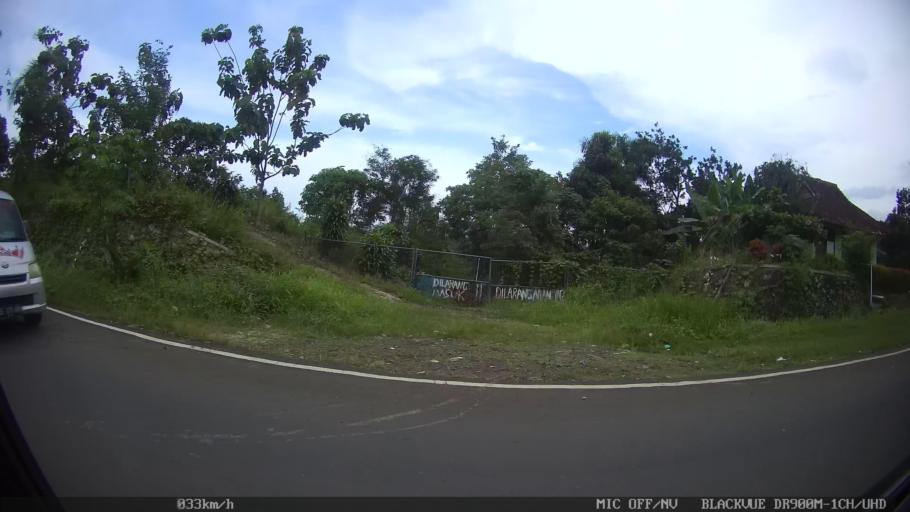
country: ID
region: Lampung
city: Bandarlampung
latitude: -5.4364
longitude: 105.2169
